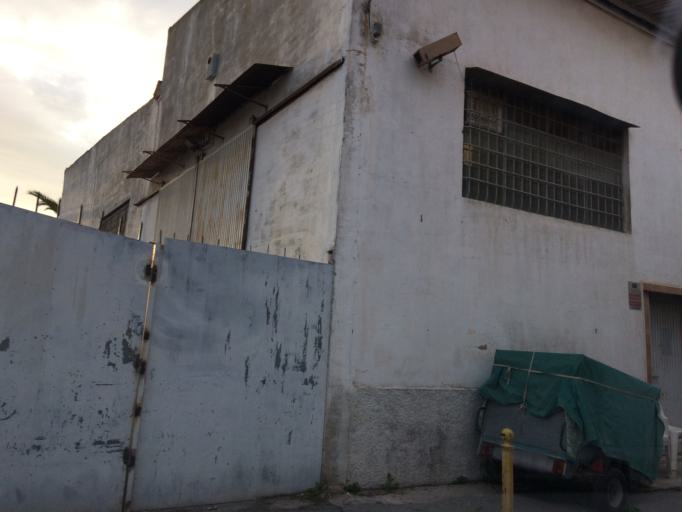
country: ES
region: Andalusia
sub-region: Provincia de Malaga
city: Malaga
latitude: 36.7075
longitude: -4.4535
